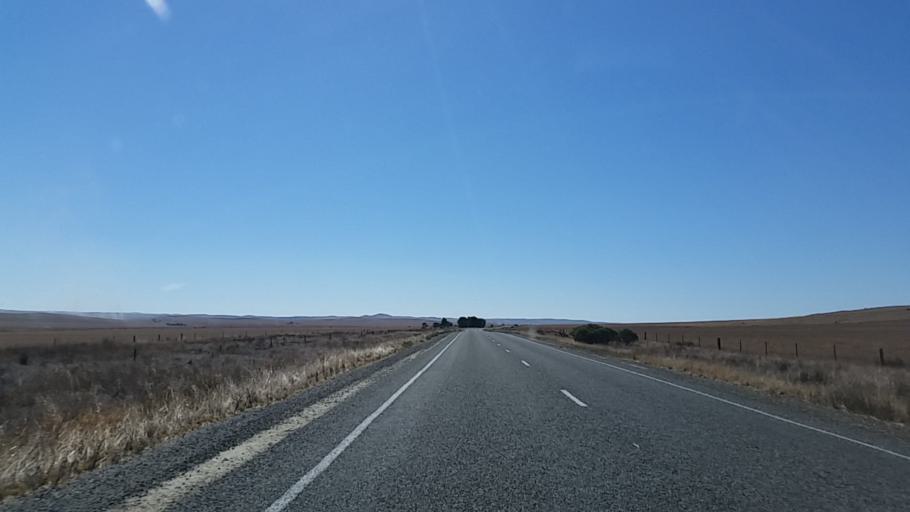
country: AU
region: South Australia
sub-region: Northern Areas
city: Jamestown
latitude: -33.3032
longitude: 138.8762
